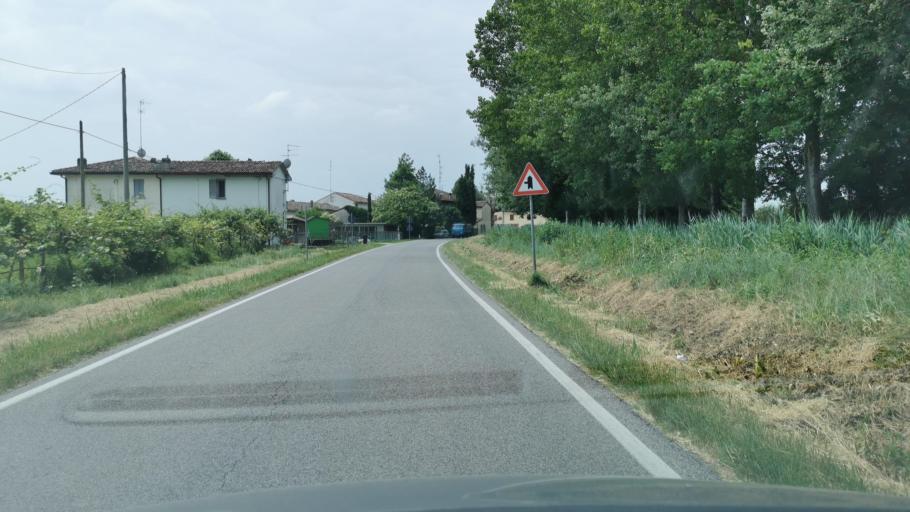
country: IT
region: Emilia-Romagna
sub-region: Provincia di Ravenna
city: Bagnacavallo
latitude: 44.4217
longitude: 11.9878
